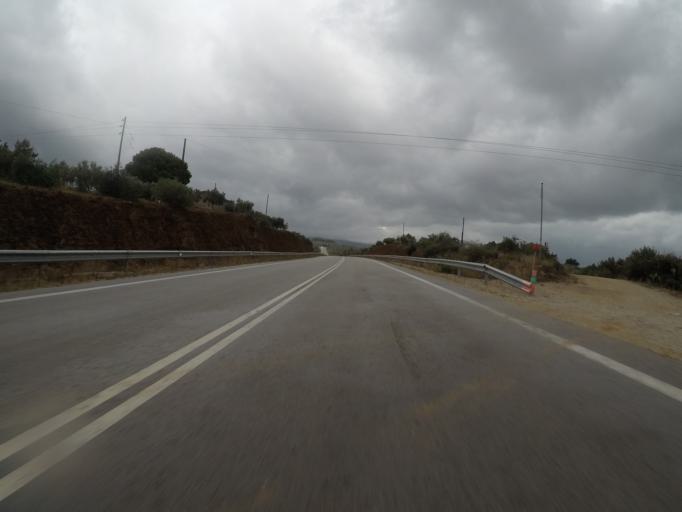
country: GR
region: Peloponnese
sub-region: Nomos Messinias
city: Gargalianoi
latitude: 37.0155
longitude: 21.6461
